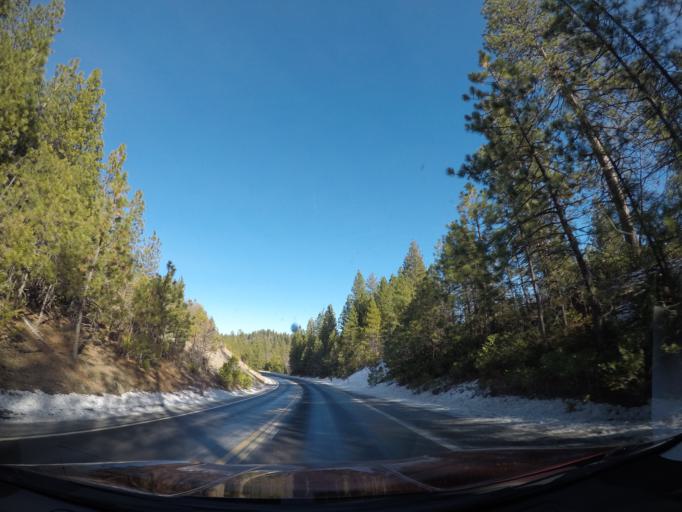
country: US
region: California
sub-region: Tuolumne County
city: Twain Harte
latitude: 38.0864
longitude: -120.1536
